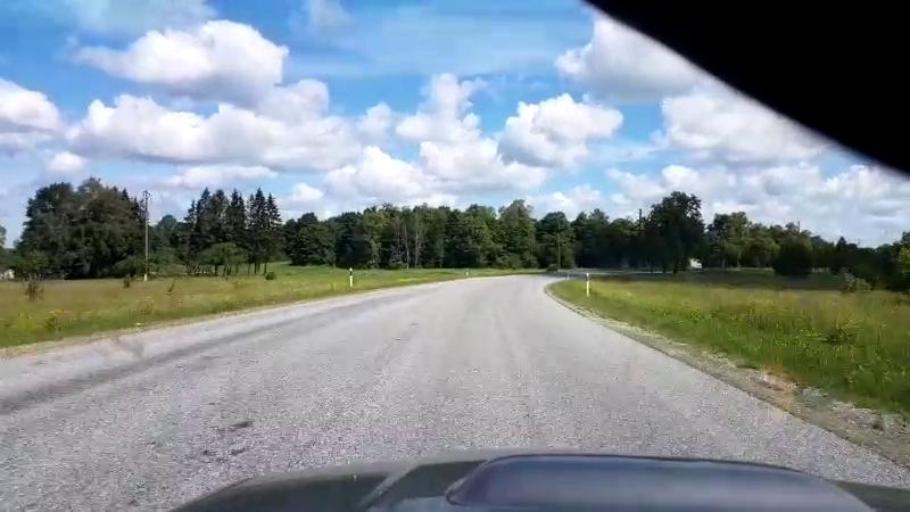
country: EE
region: Laeaene-Virumaa
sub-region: Tapa vald
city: Tapa
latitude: 59.2456
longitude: 25.9304
